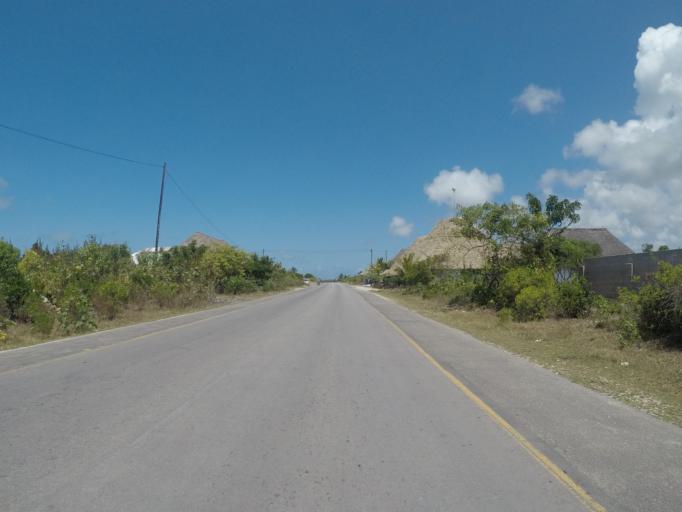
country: TZ
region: Zanzibar Central/South
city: Nganane
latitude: -6.3299
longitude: 39.5482
